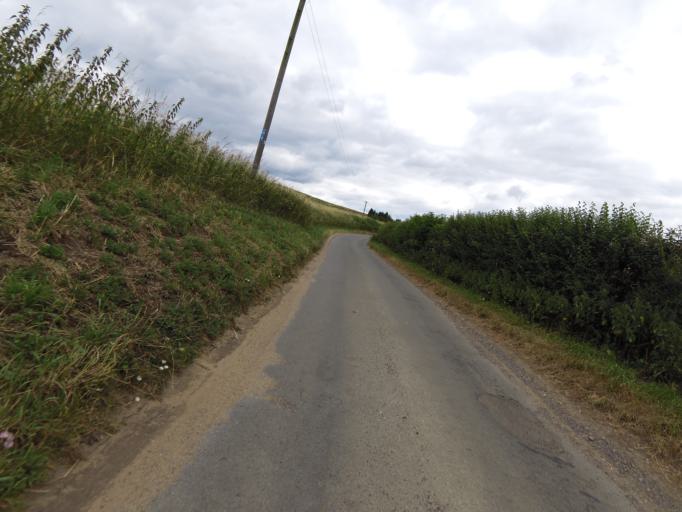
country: GB
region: England
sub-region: Norfolk
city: Harleston
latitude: 52.4040
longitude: 1.3323
